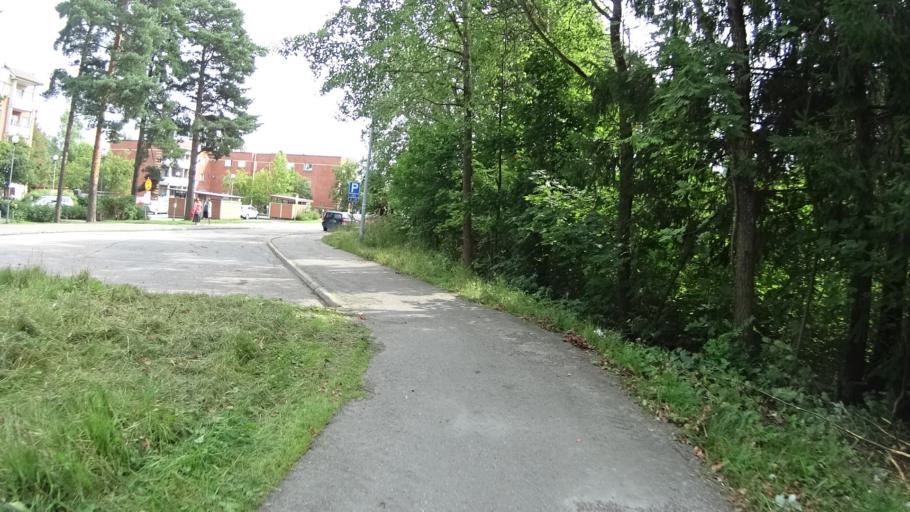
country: FI
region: Uusimaa
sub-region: Helsinki
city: Teekkarikylae
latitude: 60.2225
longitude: 24.8275
